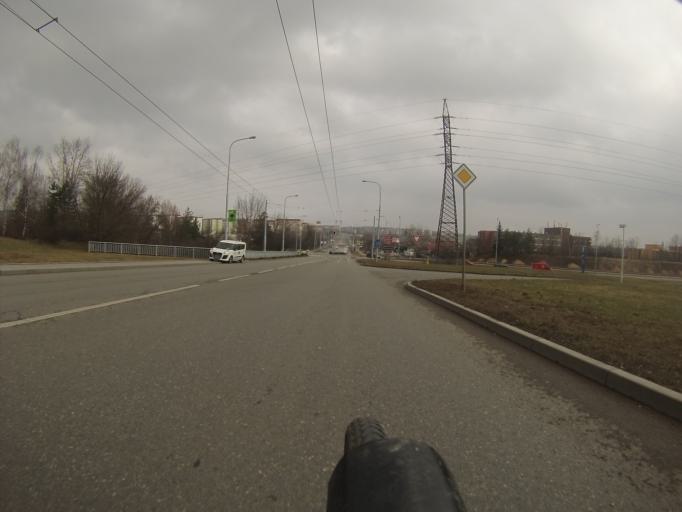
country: CZ
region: South Moravian
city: Bilovice nad Svitavou
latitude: 49.2003
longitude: 16.6644
